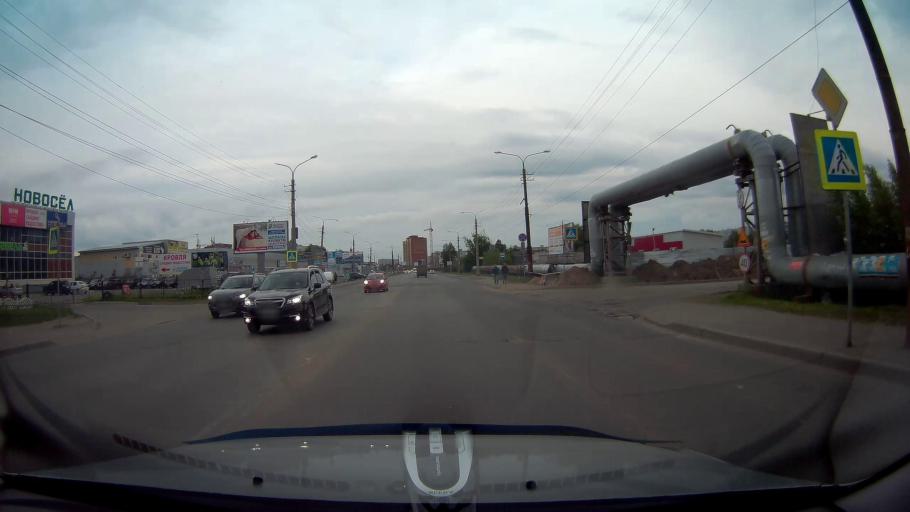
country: RU
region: Arkhangelskaya
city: Arkhangel'sk
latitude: 64.5319
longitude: 40.5998
